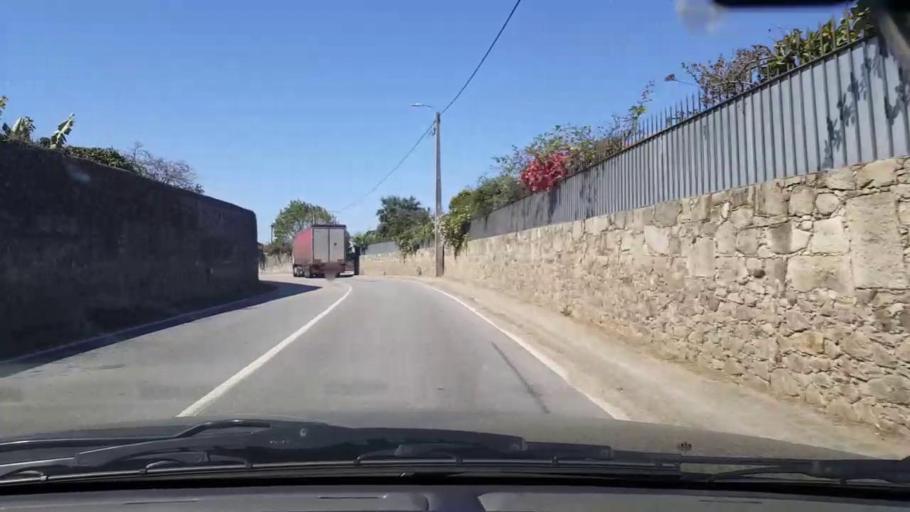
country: PT
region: Porto
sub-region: Vila do Conde
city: Arvore
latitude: 41.3410
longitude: -8.6979
